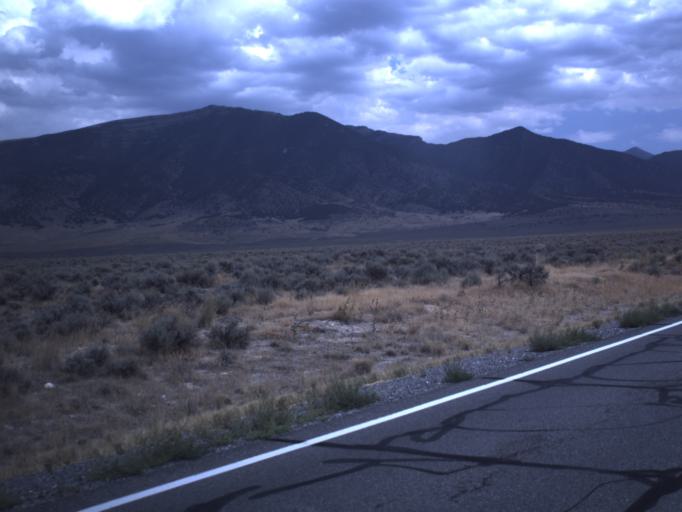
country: US
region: Utah
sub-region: Tooele County
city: Tooele
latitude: 40.3719
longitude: -112.3608
